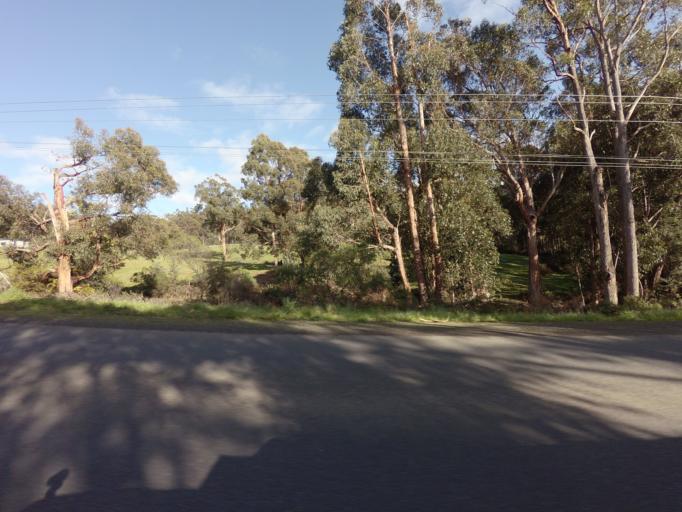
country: AU
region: Tasmania
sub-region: Huon Valley
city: Geeveston
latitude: -43.1947
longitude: 146.9570
